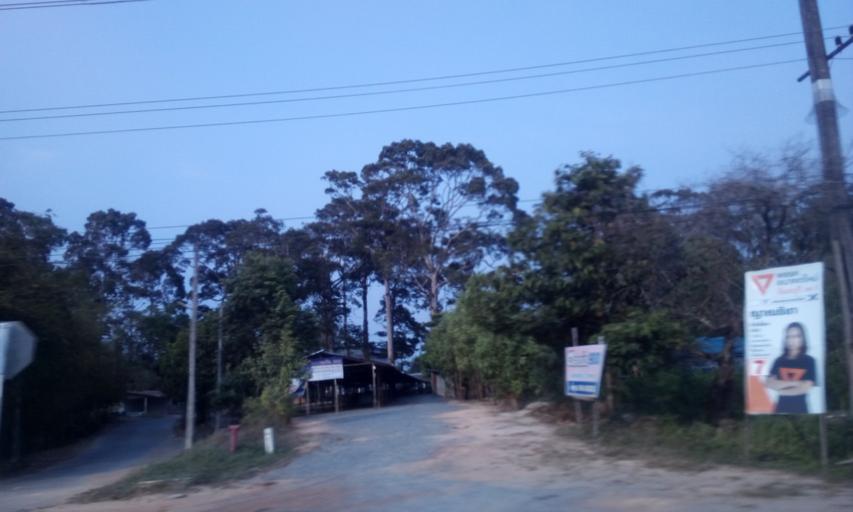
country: TH
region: Chanthaburi
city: Khlung
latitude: 12.4487
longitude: 102.2874
